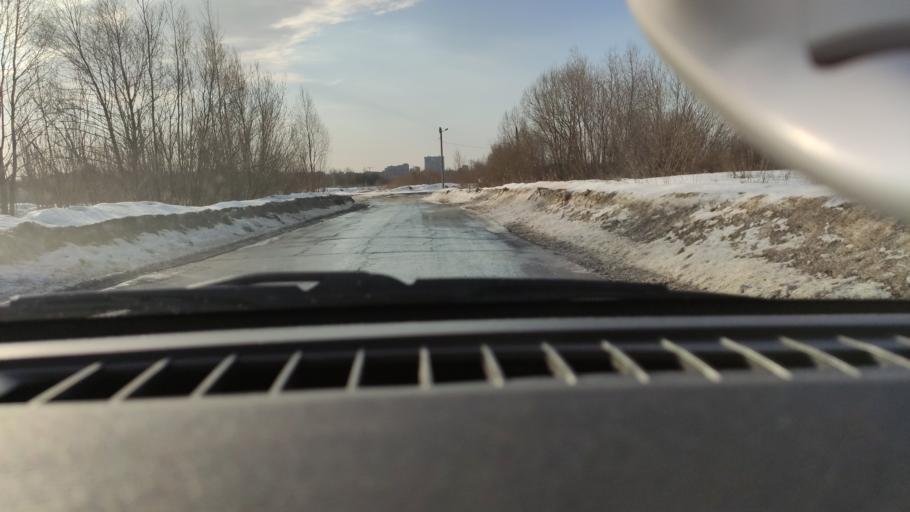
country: RU
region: Perm
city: Perm
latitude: 58.0356
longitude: 56.1910
